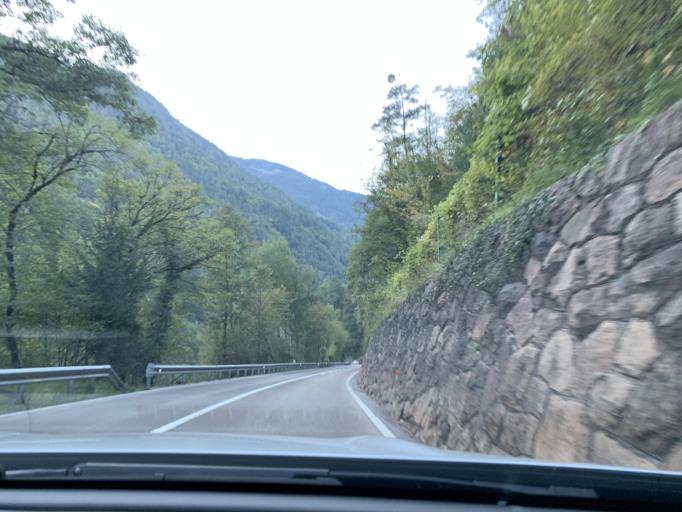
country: IT
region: Trentino-Alto Adige
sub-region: Bolzano
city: Cornedo All'Isarco
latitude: 46.4591
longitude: 11.4214
